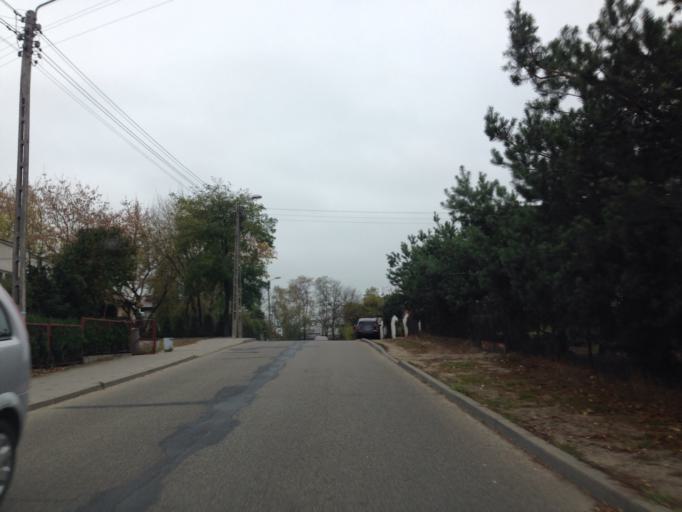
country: PL
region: Kujawsko-Pomorskie
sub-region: Powiat brodnicki
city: Brodnica
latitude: 53.2446
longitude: 19.3985
